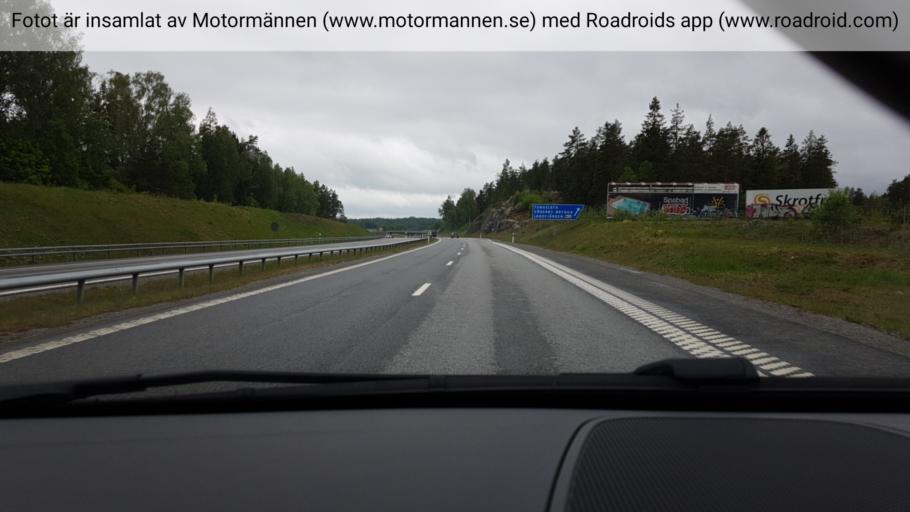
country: SE
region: Stockholm
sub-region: Haninge Kommun
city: Jordbro
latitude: 59.0744
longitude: 18.0702
